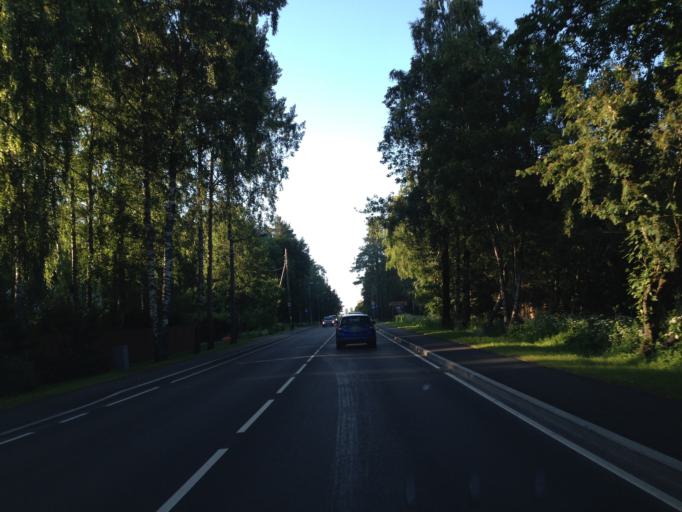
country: EE
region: Harju
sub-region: Saue vald
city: Laagri
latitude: 59.3890
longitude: 24.6416
